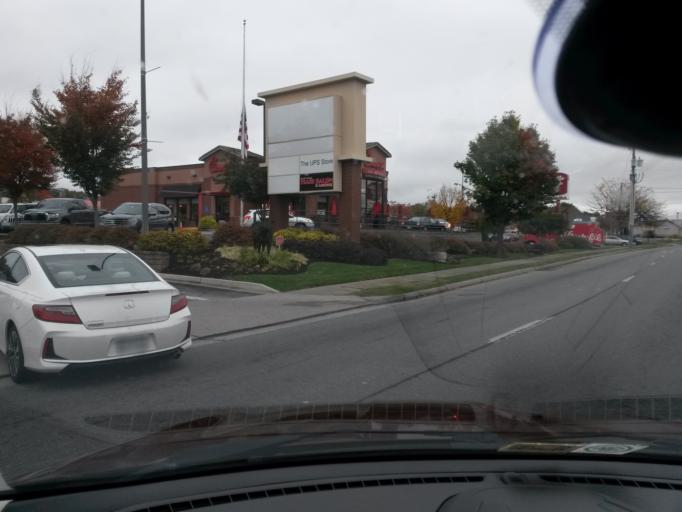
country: US
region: Virginia
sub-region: City of Salem
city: Salem
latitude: 37.2897
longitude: -80.0793
